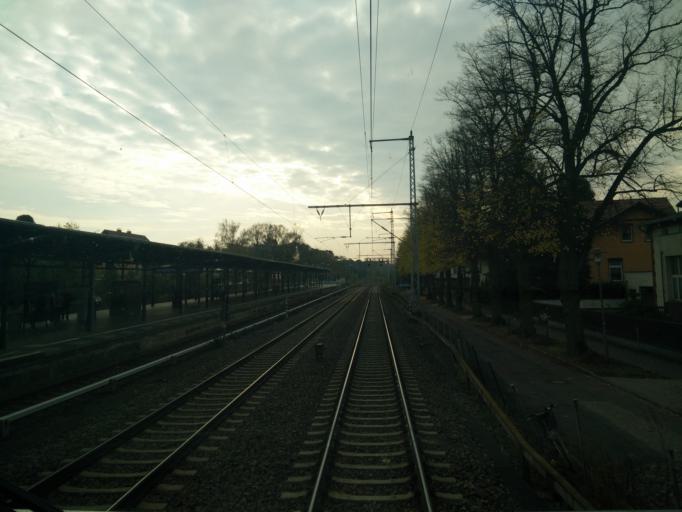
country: DE
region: Brandenburg
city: Zeuthen
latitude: 52.3492
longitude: 13.6269
